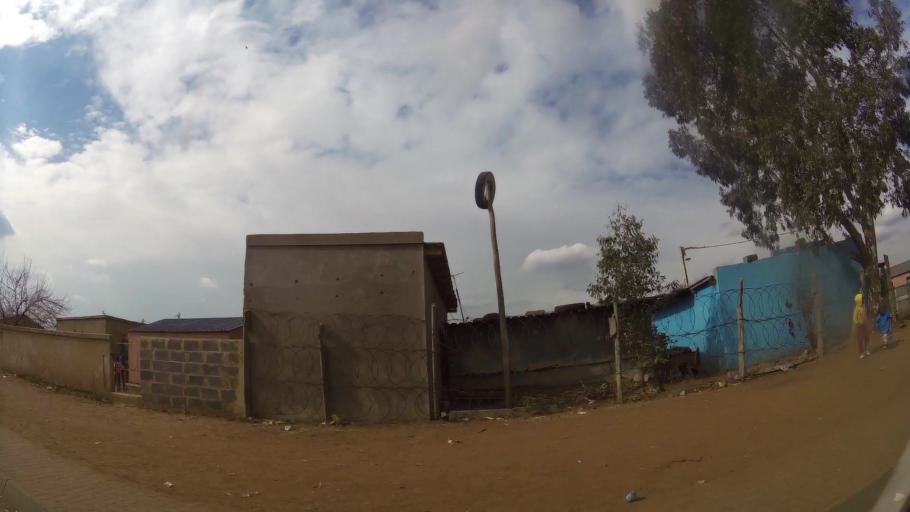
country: ZA
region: Gauteng
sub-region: Ekurhuleni Metropolitan Municipality
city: Germiston
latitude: -26.4046
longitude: 28.1638
